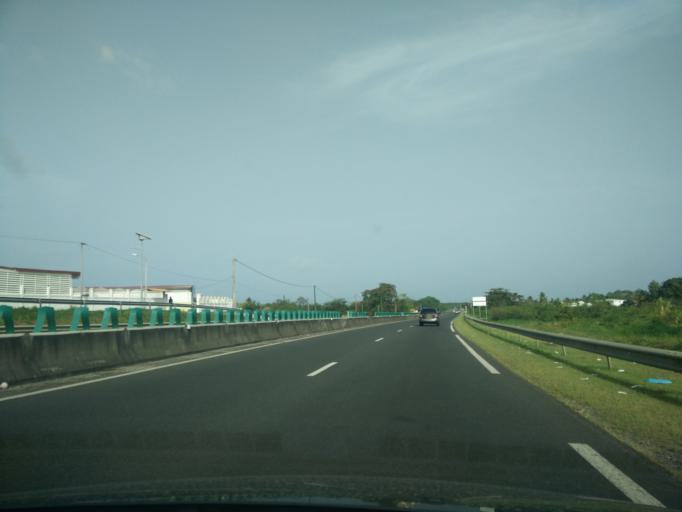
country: GP
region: Guadeloupe
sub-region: Guadeloupe
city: Petit-Bourg
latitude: 16.1801
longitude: -61.5979
